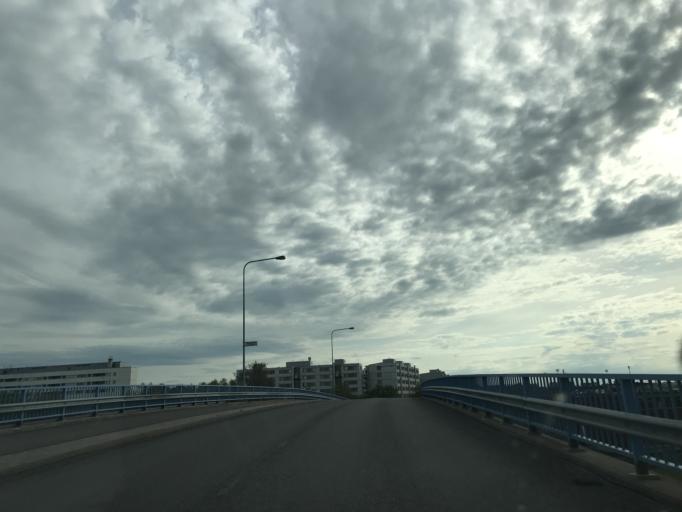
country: FI
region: Varsinais-Suomi
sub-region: Turku
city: Turku
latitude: 60.4450
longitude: 22.3079
